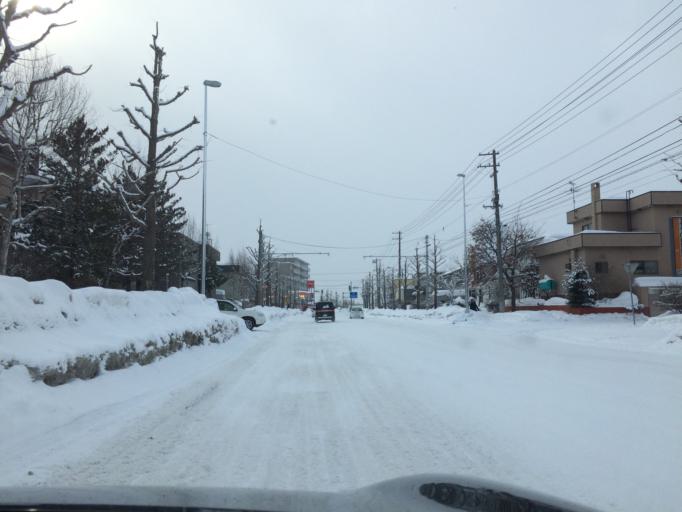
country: JP
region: Hokkaido
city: Ebetsu
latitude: 43.0536
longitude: 141.4756
